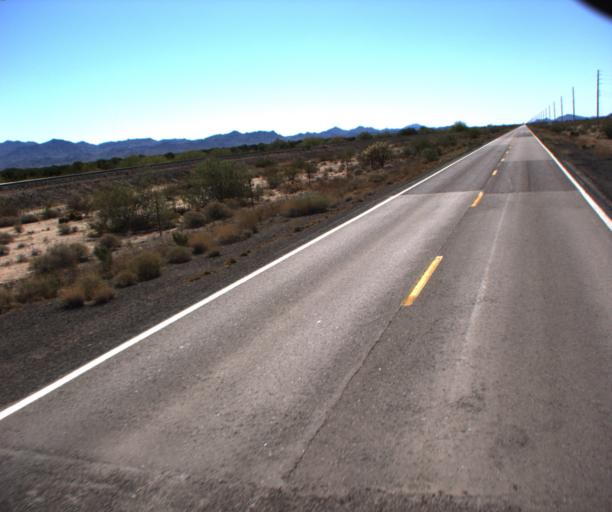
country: US
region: Arizona
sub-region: La Paz County
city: Salome
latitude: 33.8278
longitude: -113.8721
